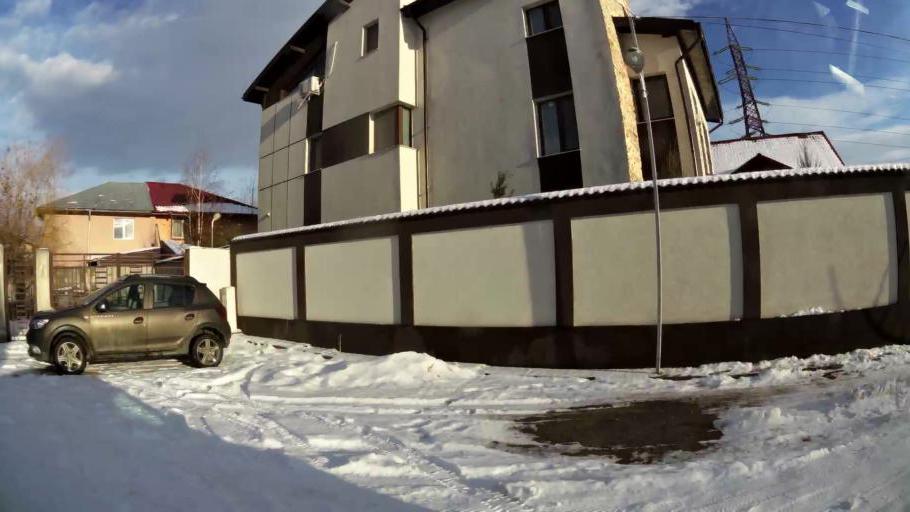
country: RO
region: Ilfov
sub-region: Comuna Fundeni-Dobroesti
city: Fundeni
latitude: 44.4611
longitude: 26.1742
